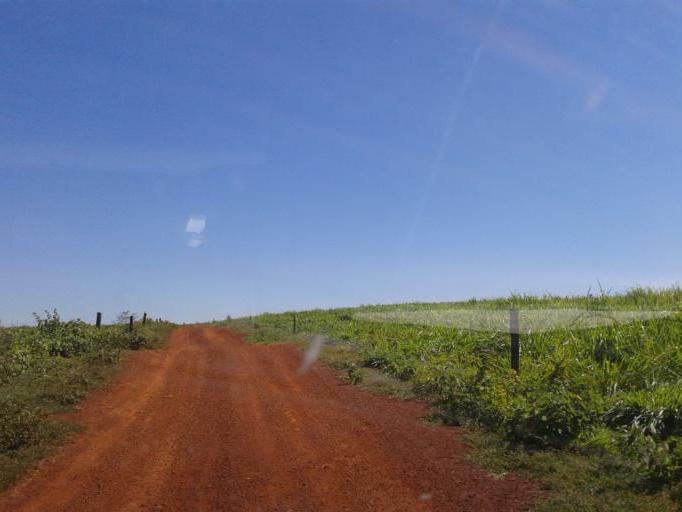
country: BR
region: Minas Gerais
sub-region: Capinopolis
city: Capinopolis
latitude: -18.6280
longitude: -49.6123
